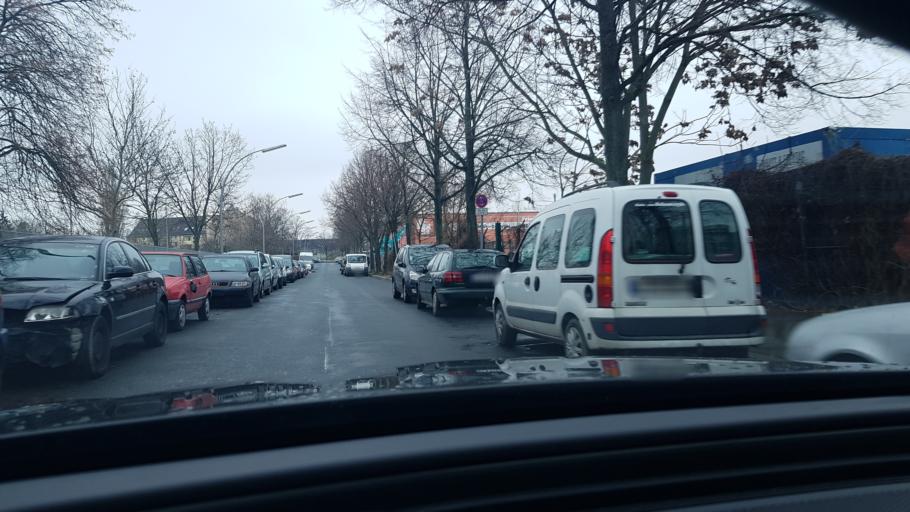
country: DE
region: Berlin
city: Tempelhof Bezirk
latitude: 52.4602
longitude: 13.4026
